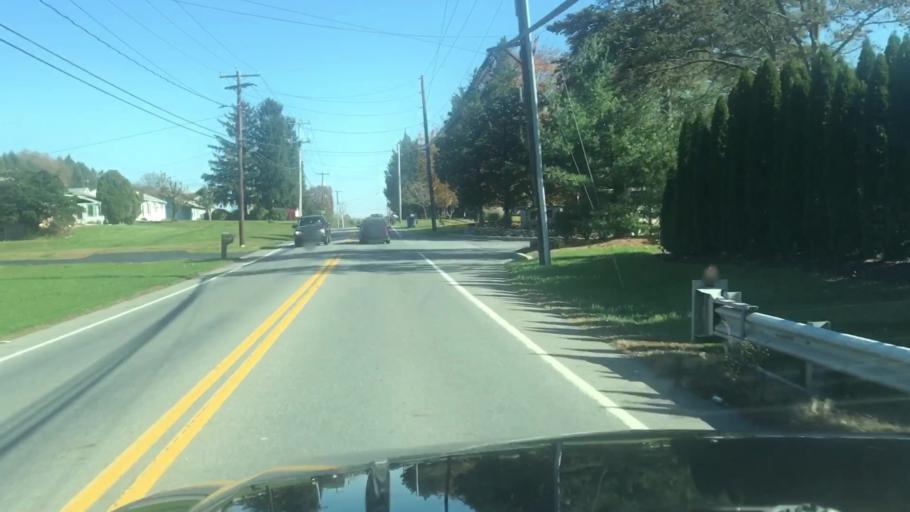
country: US
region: Pennsylvania
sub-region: Cumberland County
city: Enola
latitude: 40.2880
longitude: -76.9982
